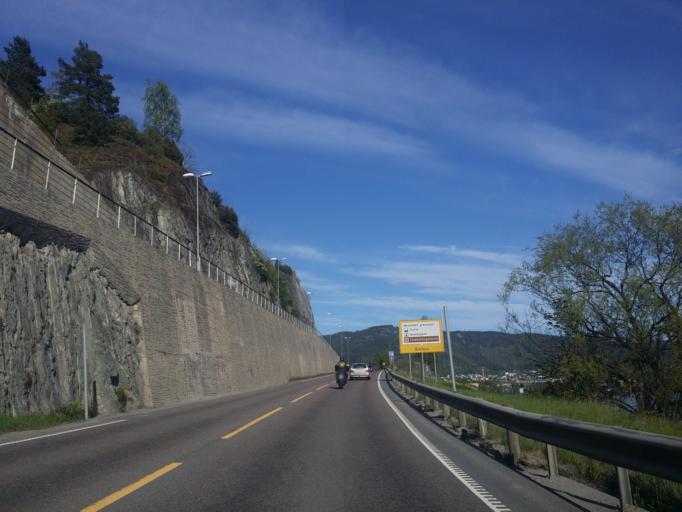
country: NO
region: Telemark
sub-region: Notodden
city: Notodden
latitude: 59.5611
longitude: 9.2366
